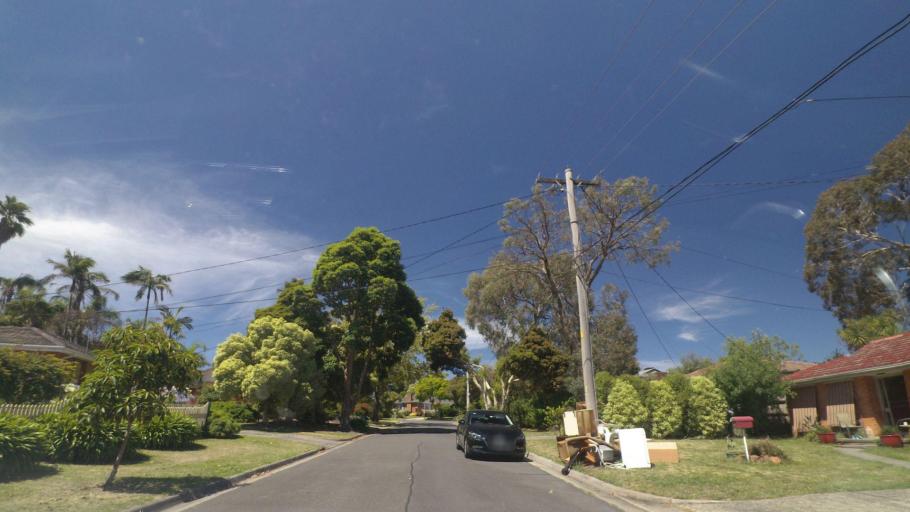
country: AU
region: Victoria
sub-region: Maroondah
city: Ringwood East
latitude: -37.8022
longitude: 145.2277
